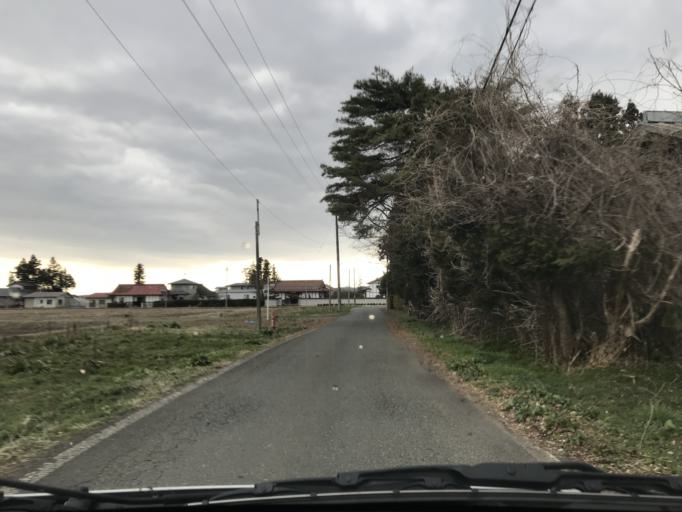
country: JP
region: Iwate
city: Mizusawa
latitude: 39.0761
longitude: 141.1613
